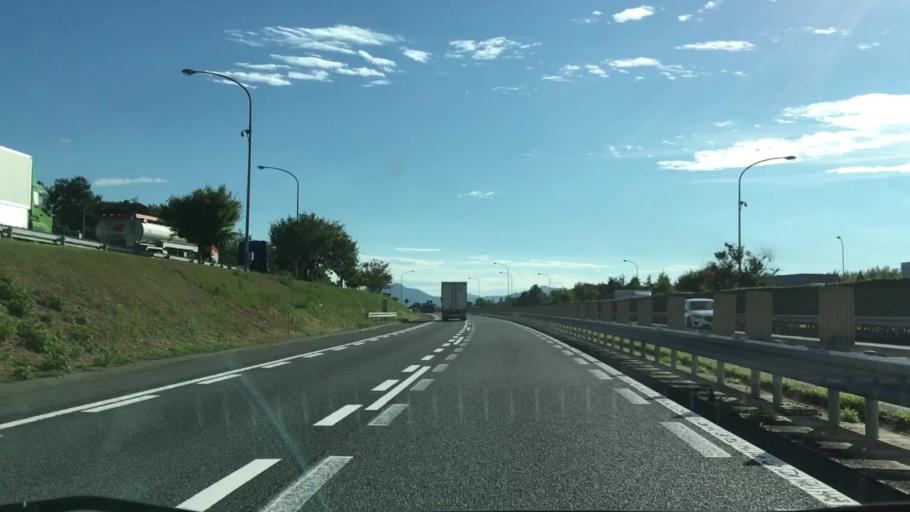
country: JP
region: Yamaguchi
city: Iwakuni
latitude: 34.1001
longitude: 132.1024
